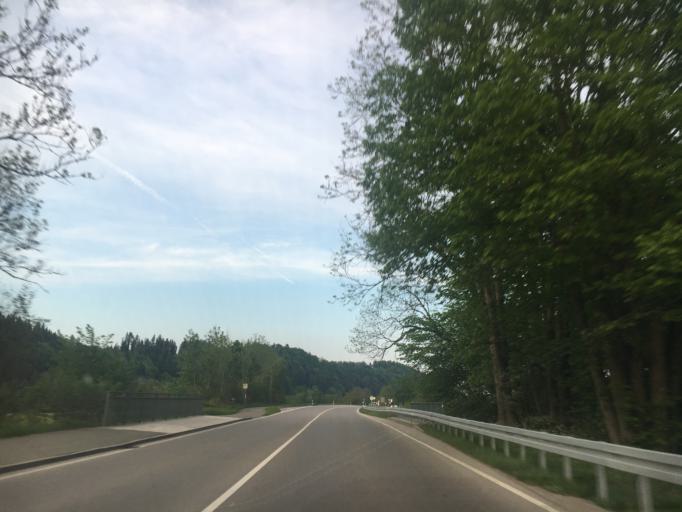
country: DE
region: Bavaria
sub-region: Upper Bavaria
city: Bad Heilbrunn
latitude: 47.7478
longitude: 11.4827
